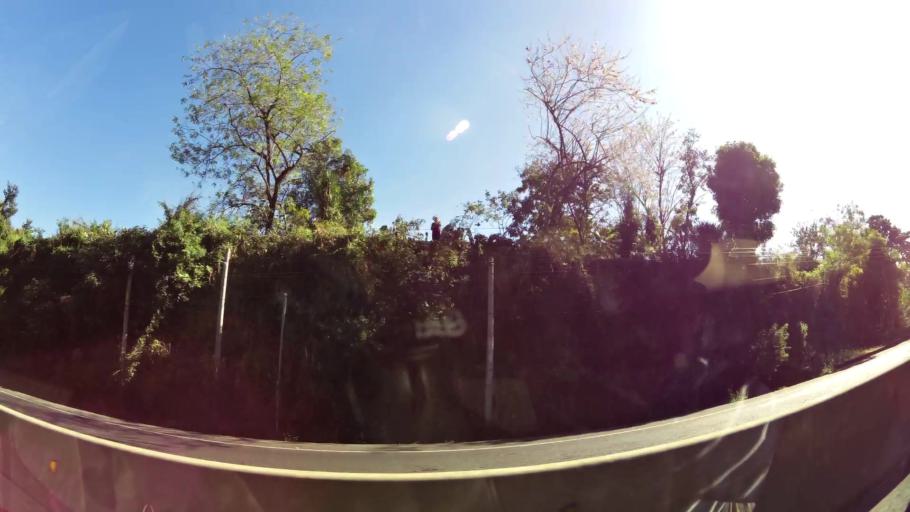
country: SV
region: Santa Ana
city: Coatepeque
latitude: 13.9238
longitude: -89.5195
